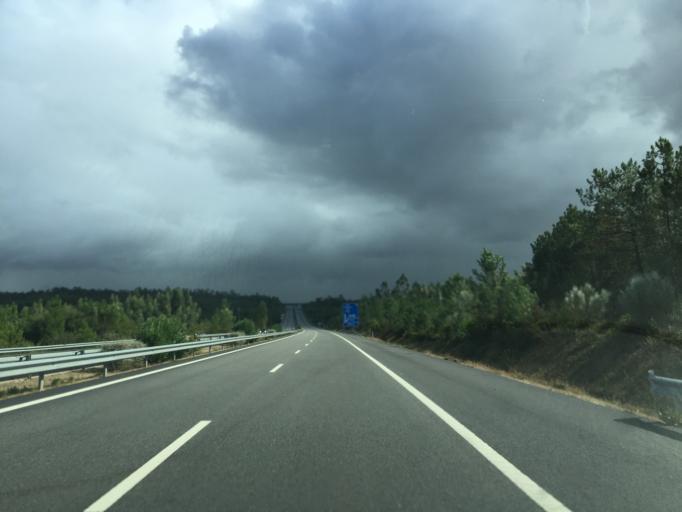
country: PT
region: Coimbra
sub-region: Cantanhede
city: Cantanhede
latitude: 40.2838
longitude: -8.5442
